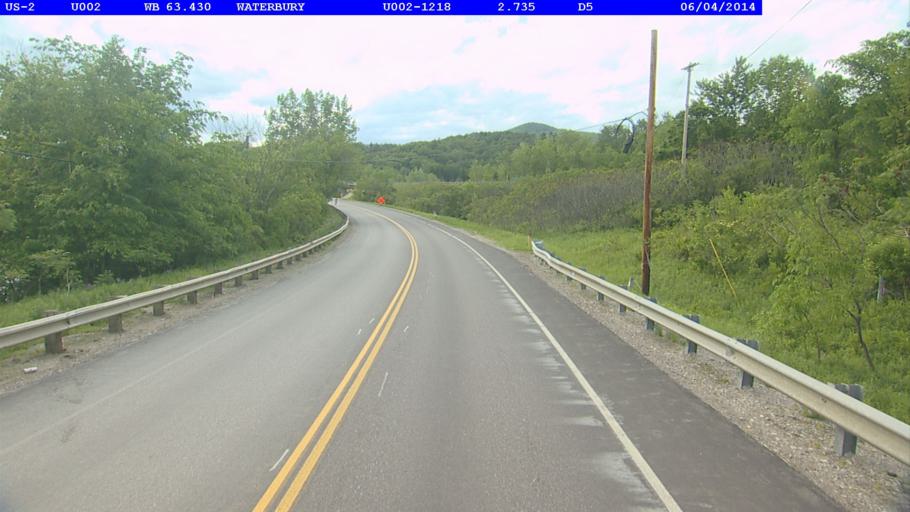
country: US
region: Vermont
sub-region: Washington County
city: Waterbury
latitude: 44.3509
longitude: -72.7754
